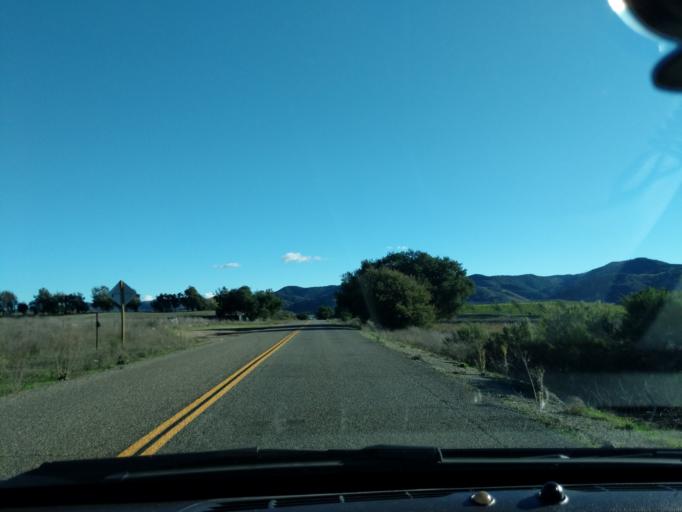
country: US
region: California
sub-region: Santa Barbara County
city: Los Alamos
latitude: 34.7569
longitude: -120.2966
